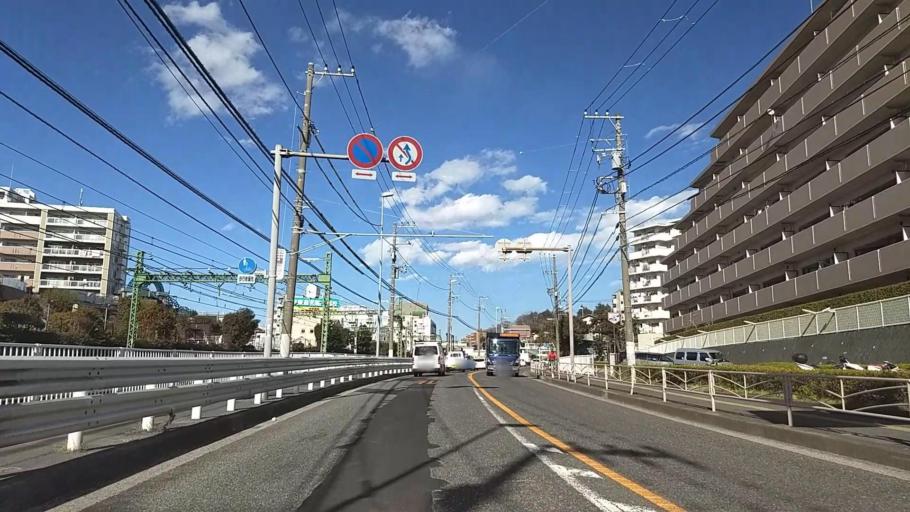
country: JP
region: Kanagawa
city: Zushi
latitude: 35.3580
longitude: 139.6282
